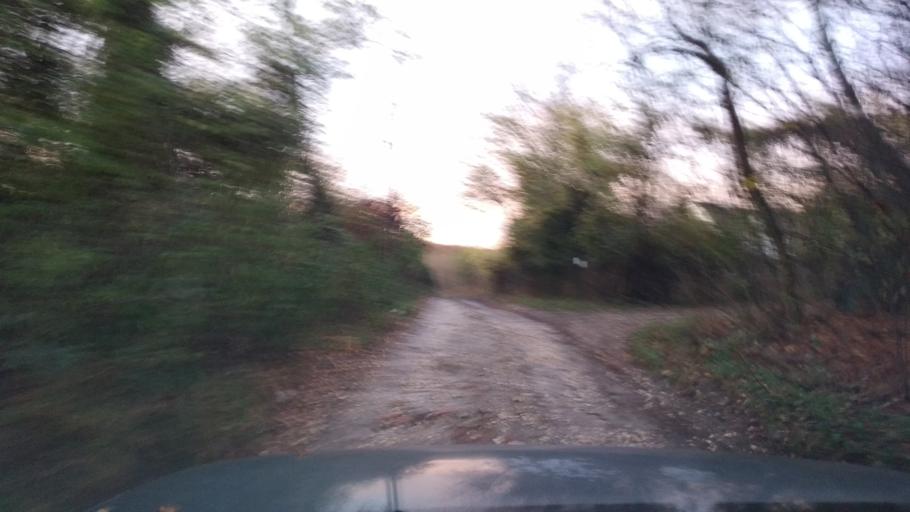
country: HU
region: Pest
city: Nagykovacsi
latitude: 47.6617
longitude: 18.9989
